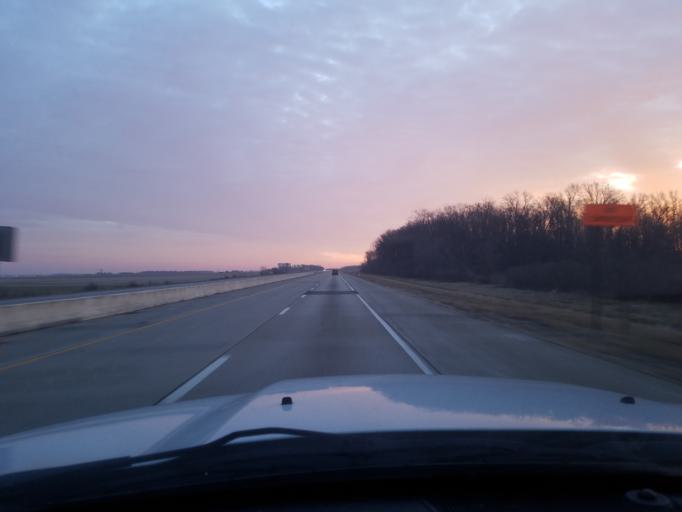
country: US
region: Indiana
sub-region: Wells County
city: Ossian
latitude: 40.9520
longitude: -85.2404
